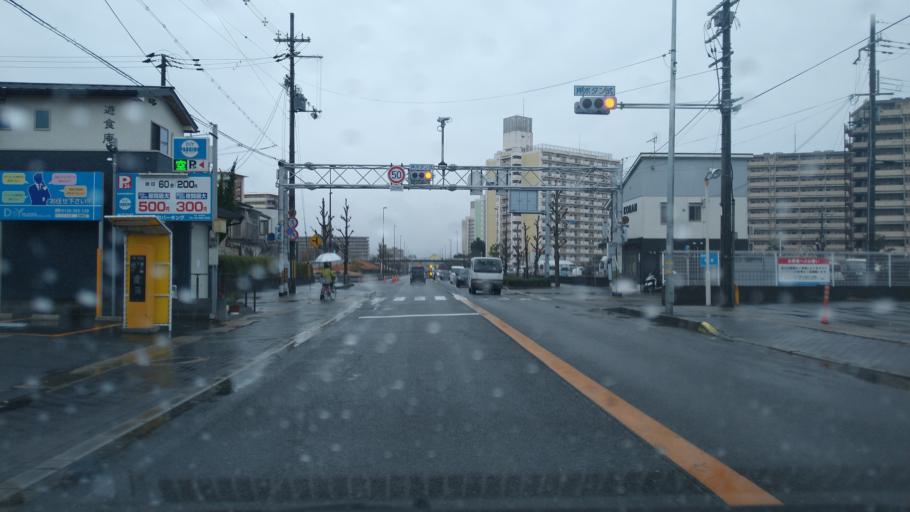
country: JP
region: Kyoto
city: Uji
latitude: 34.9214
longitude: 135.7743
